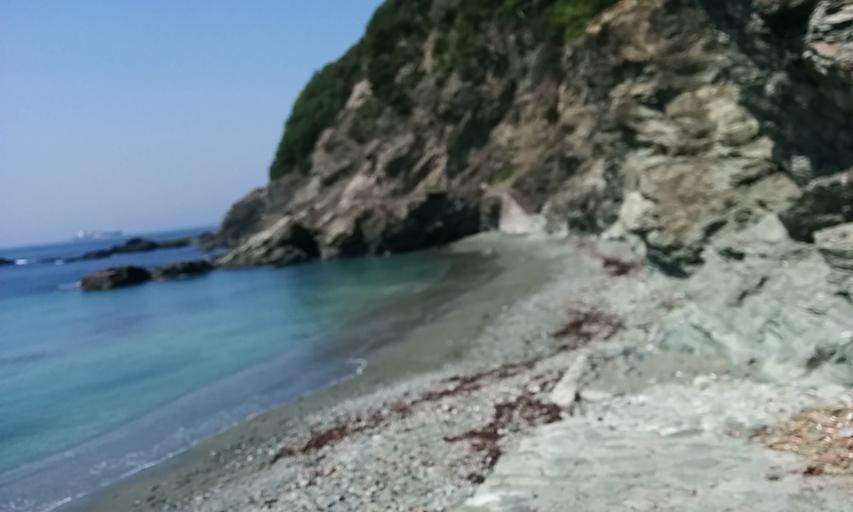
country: JP
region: Oita
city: Tsukumiura
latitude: 33.3449
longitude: 132.0180
